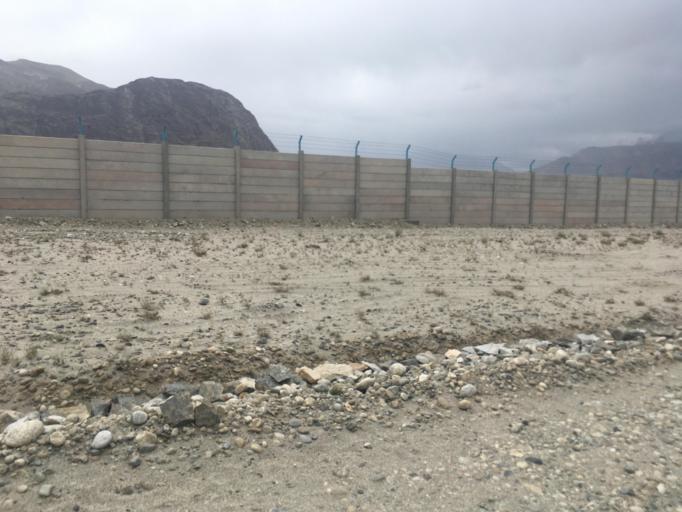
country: PK
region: Gilgit-Baltistan
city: Skardu
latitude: 35.3133
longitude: 75.6578
